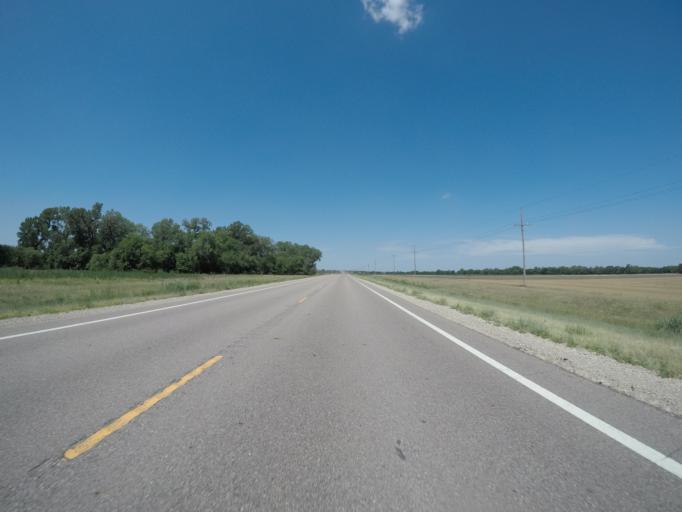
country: US
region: Kansas
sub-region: Osborne County
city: Osborne
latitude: 39.5097
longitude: -98.6155
